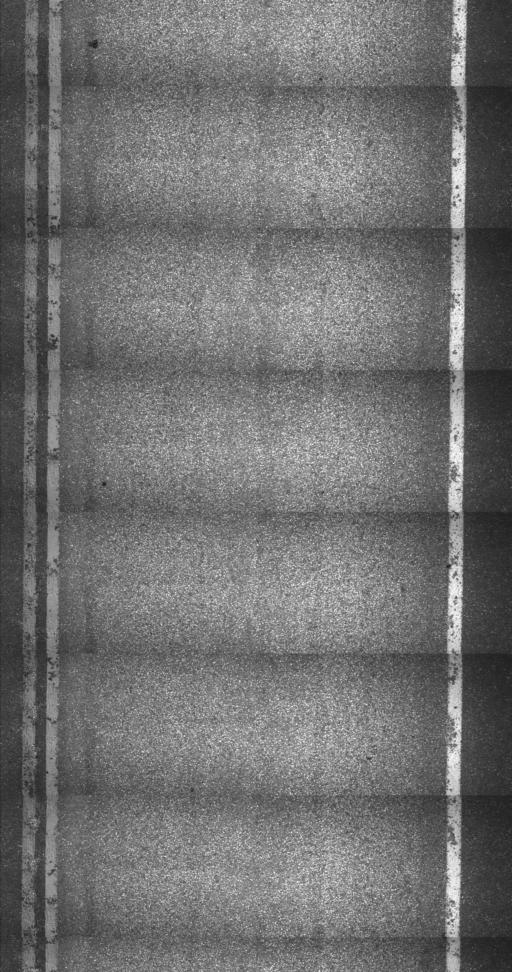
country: US
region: New York
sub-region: Clinton County
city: Rouses Point
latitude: 44.9406
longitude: -73.2749
